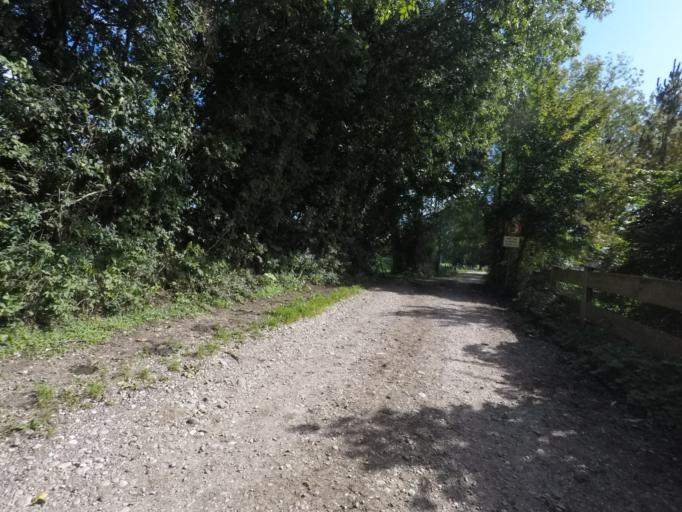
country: DE
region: Bavaria
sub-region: Upper Bavaria
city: Bad Toelz
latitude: 47.8023
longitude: 11.5657
